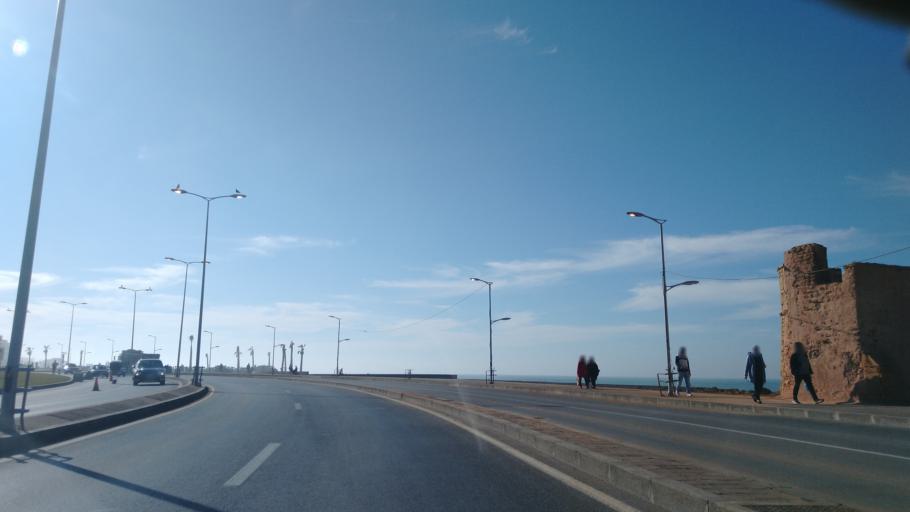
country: MA
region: Rabat-Sale-Zemmour-Zaer
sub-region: Rabat
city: Rabat
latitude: 34.0308
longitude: -6.8441
